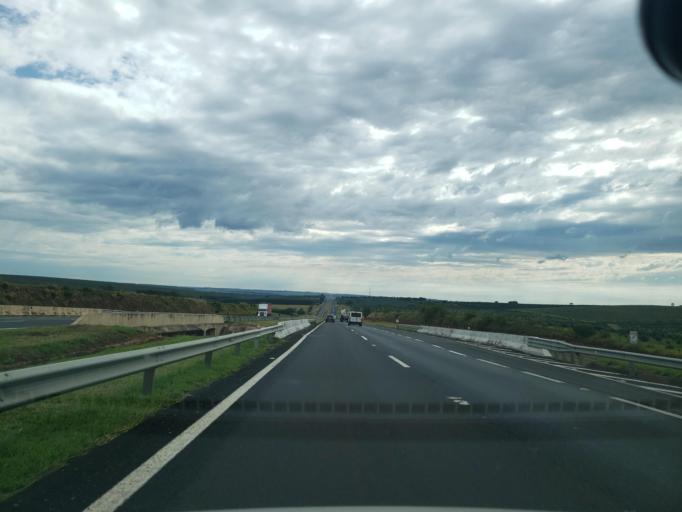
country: BR
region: Sao Paulo
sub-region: Bauru
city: Bauru
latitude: -22.1837
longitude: -49.2167
